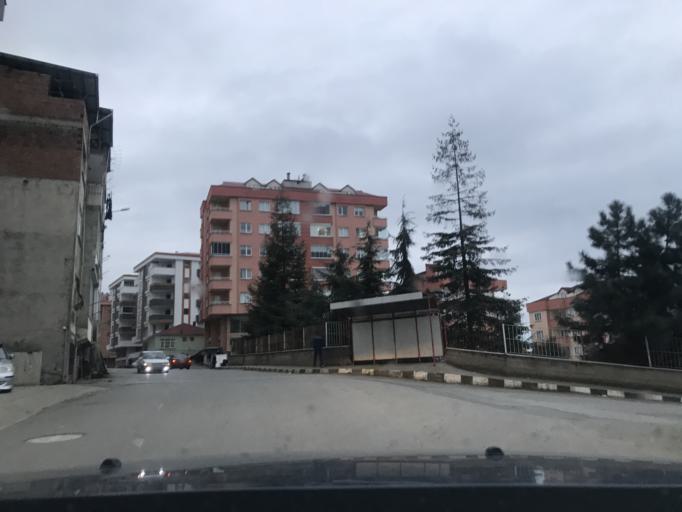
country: TR
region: Trabzon
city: Akcaabat
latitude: 41.0136
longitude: 39.5887
